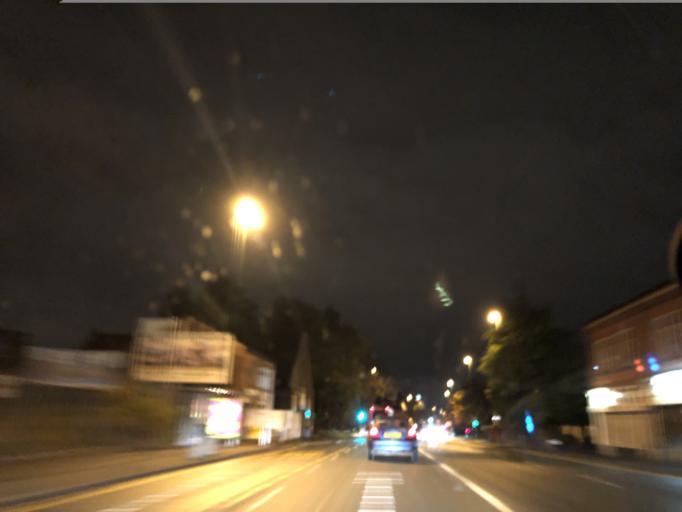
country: GB
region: England
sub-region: Manchester
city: Failsworth
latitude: 53.5075
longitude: -2.1651
